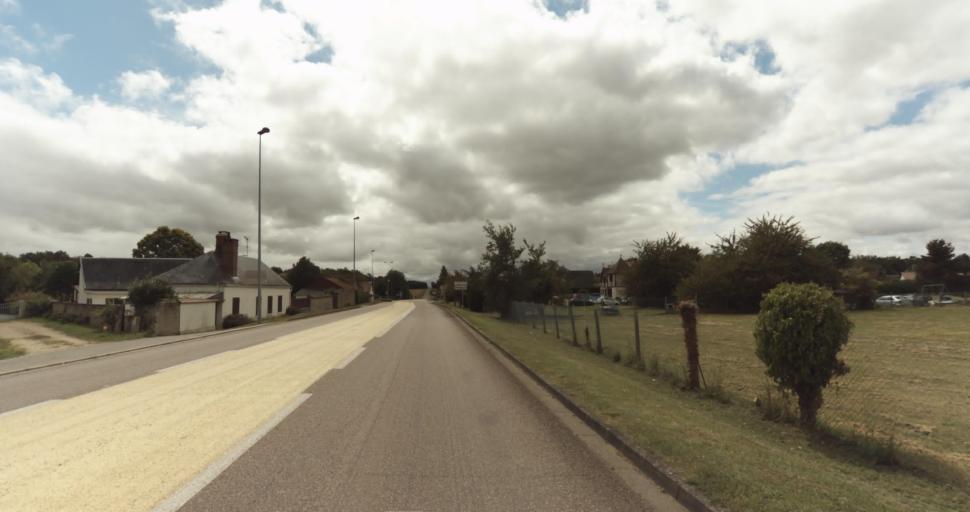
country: FR
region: Haute-Normandie
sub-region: Departement de l'Eure
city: Evreux
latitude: 48.9733
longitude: 1.1591
